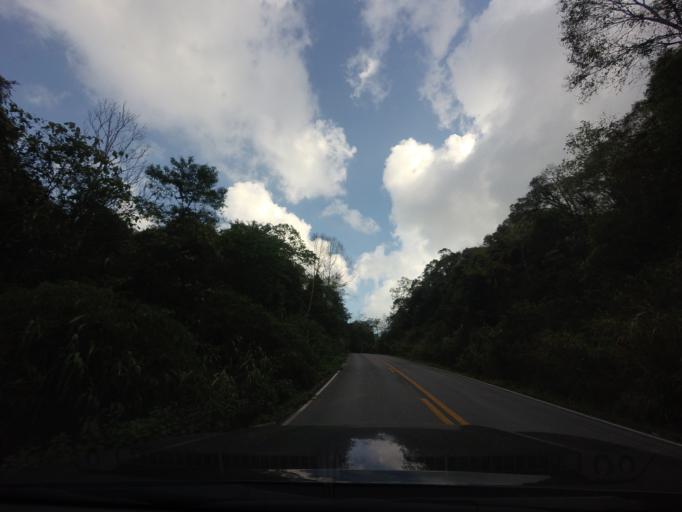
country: TH
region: Phetchabun
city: Lom Kao
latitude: 16.9355
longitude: 101.0417
